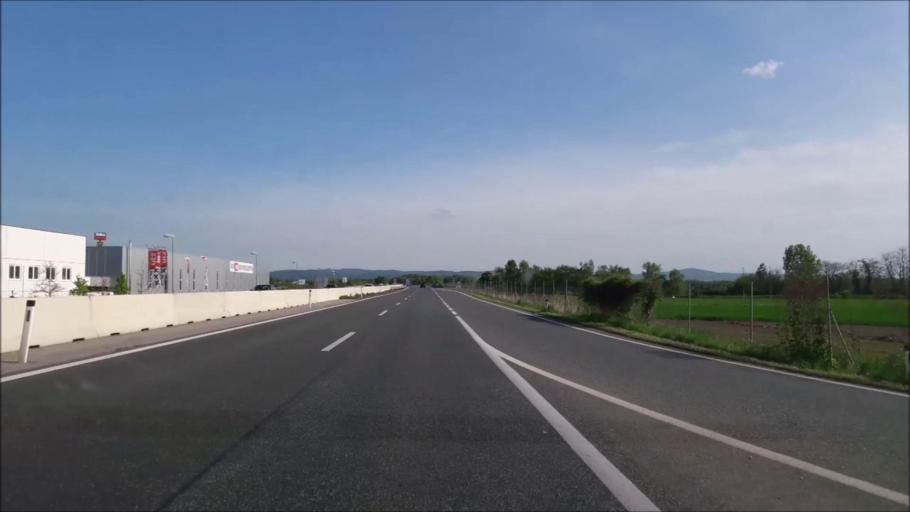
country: AT
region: Lower Austria
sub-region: Politischer Bezirk Korneuburg
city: Sierndorf
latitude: 48.3926
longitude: 16.1760
